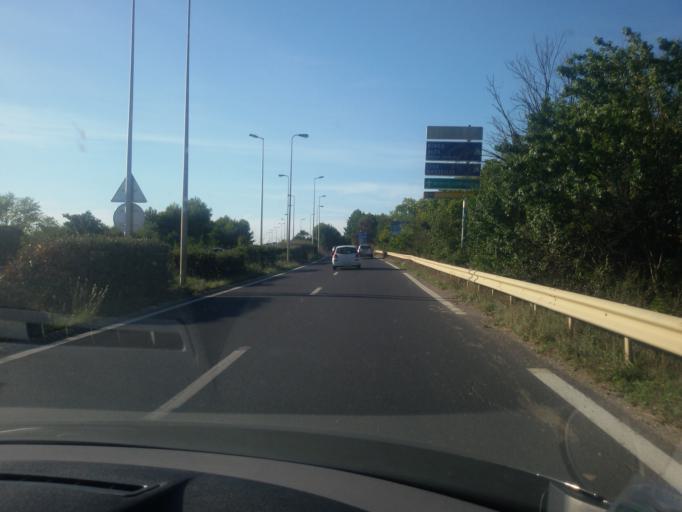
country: FR
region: Languedoc-Roussillon
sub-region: Departement de l'Herault
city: Lattes
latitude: 43.5849
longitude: 3.8965
